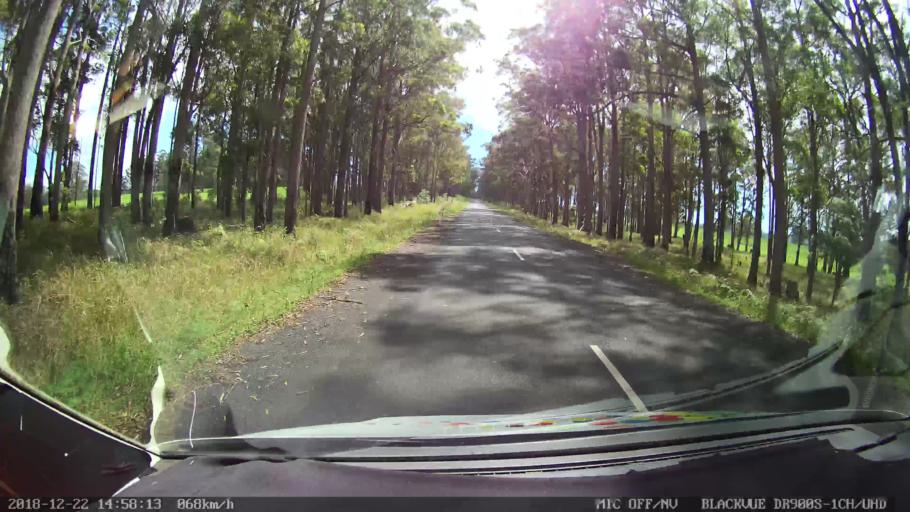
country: AU
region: New South Wales
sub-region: Bellingen
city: Dorrigo
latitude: -30.2388
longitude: 152.4933
